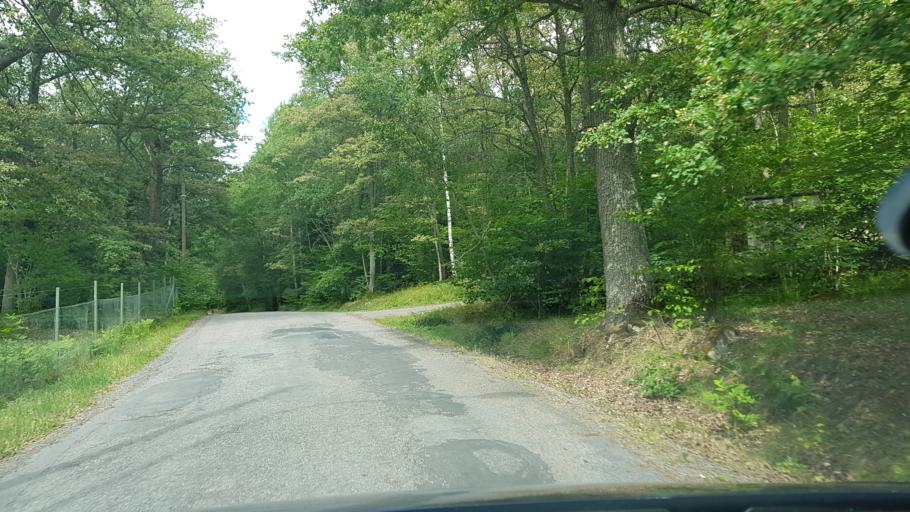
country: SE
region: Stockholm
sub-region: Upplands-Bro Kommun
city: Kungsaengen
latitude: 59.4950
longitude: 17.8062
